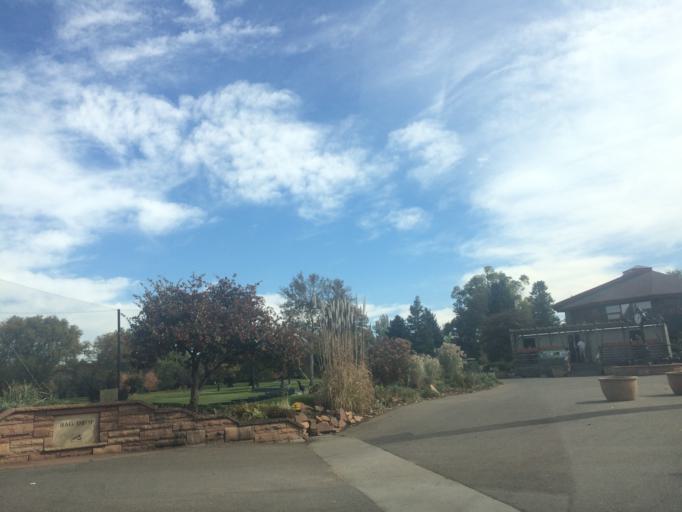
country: US
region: Colorado
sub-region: Boulder County
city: Boulder
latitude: 40.0117
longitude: -105.2208
